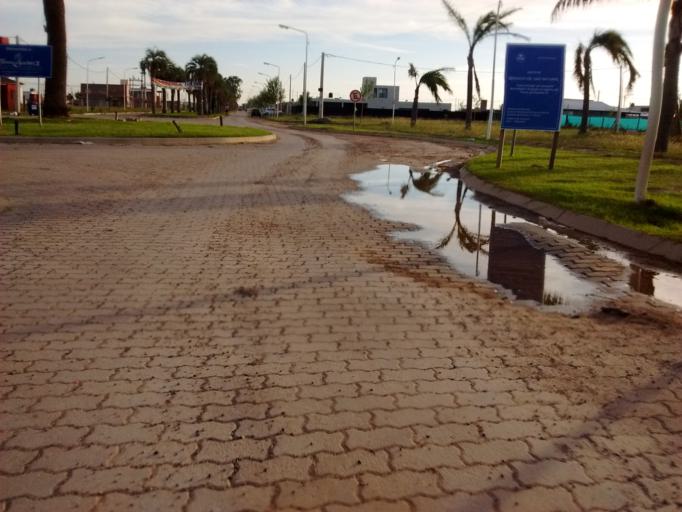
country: AR
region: Santa Fe
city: Roldan
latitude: -32.9309
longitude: -60.8755
